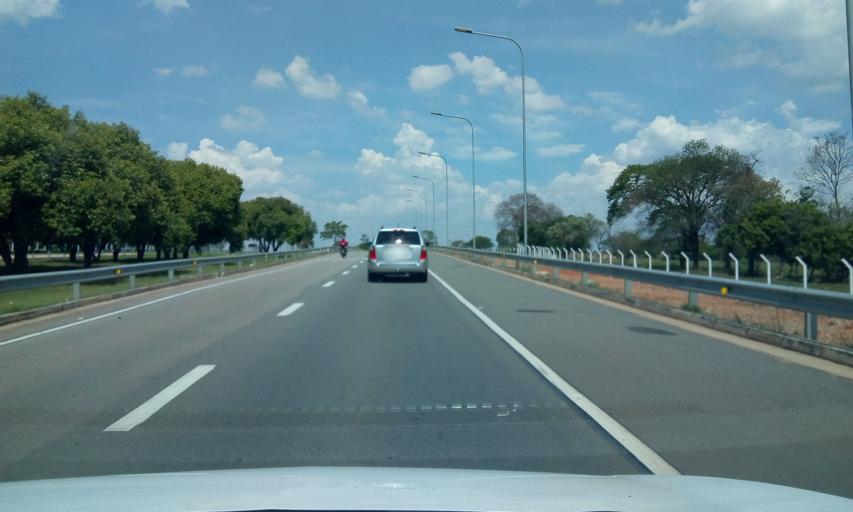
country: BR
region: Sao Paulo
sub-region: Indaiatuba
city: Indaiatuba
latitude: -23.0202
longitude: -47.1329
